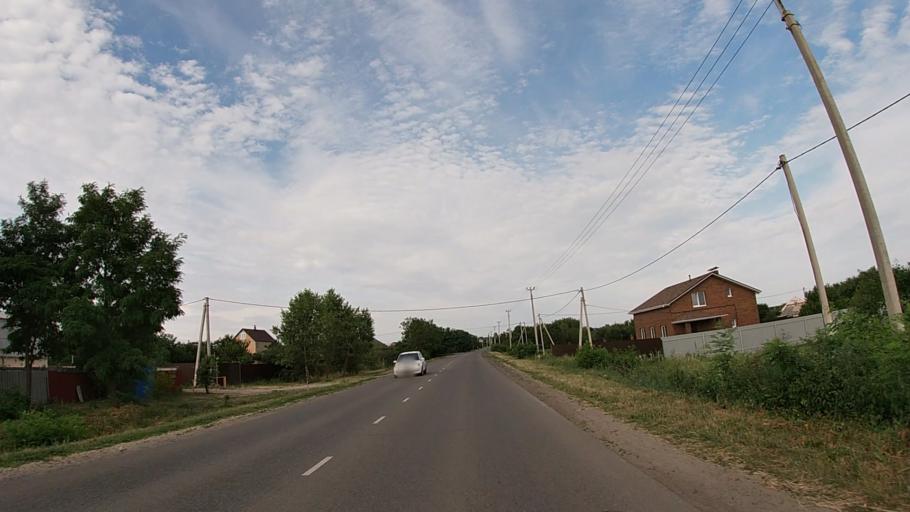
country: RU
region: Belgorod
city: Severnyy
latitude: 50.6963
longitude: 36.5736
